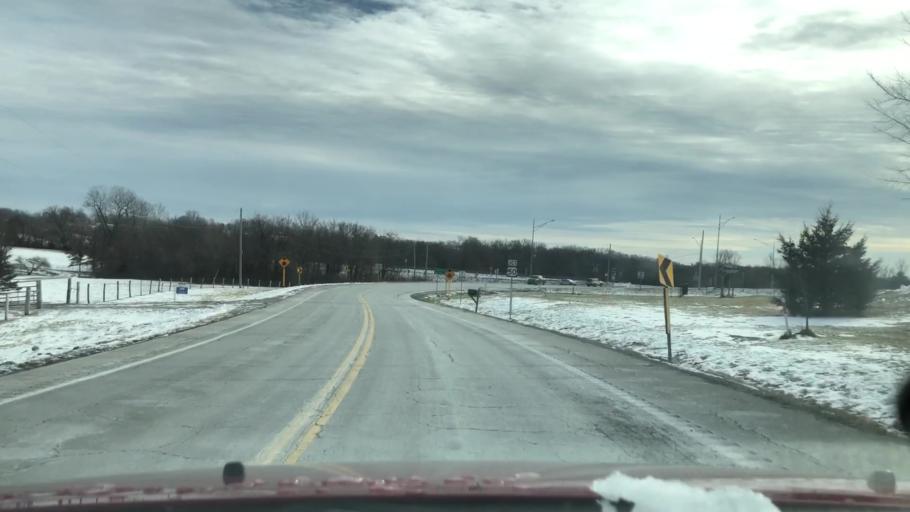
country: US
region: Missouri
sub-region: Jackson County
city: Lone Jack
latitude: 38.8719
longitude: -94.1347
